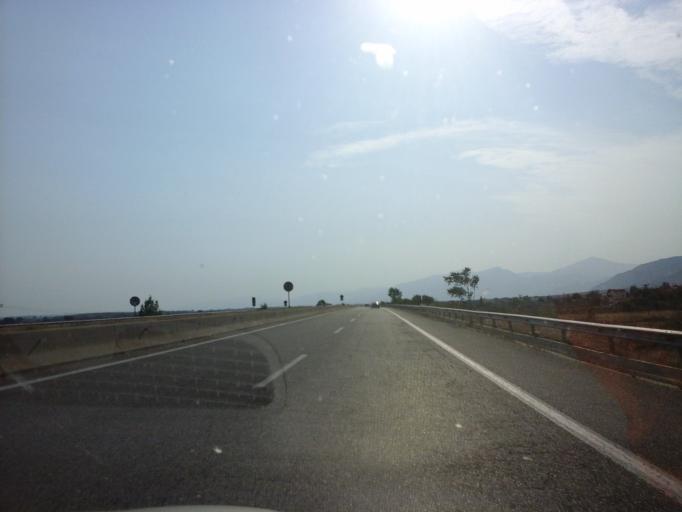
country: GR
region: East Macedonia and Thrace
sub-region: Nomos Xanthis
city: Selero
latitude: 41.1205
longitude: 25.0705
